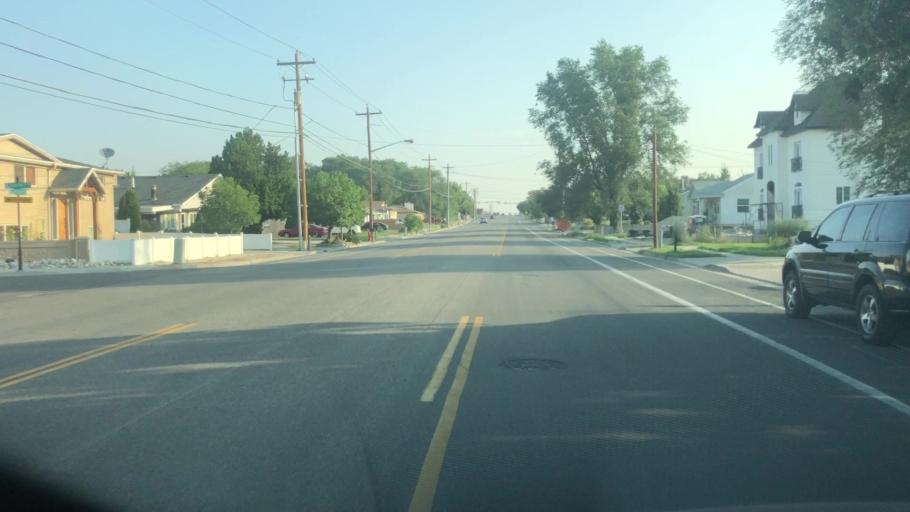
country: US
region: Utah
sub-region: Salt Lake County
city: South Jordan
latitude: 40.5580
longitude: -111.9292
